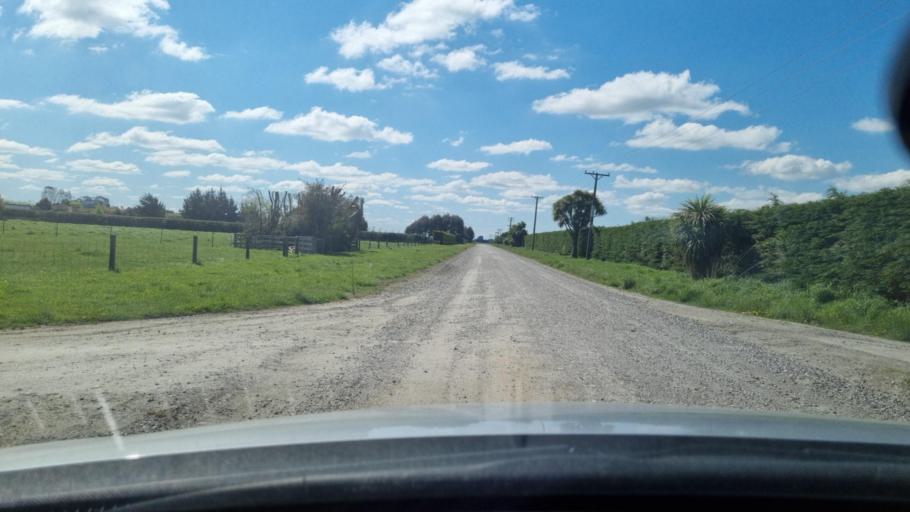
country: NZ
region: Southland
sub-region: Invercargill City
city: Invercargill
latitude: -46.3753
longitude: 168.2985
